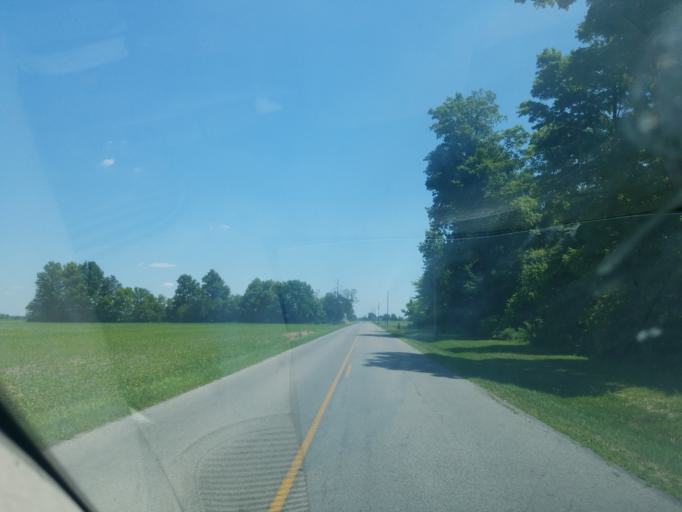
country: US
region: Ohio
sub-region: Allen County
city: Elida
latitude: 40.7872
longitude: -84.2658
